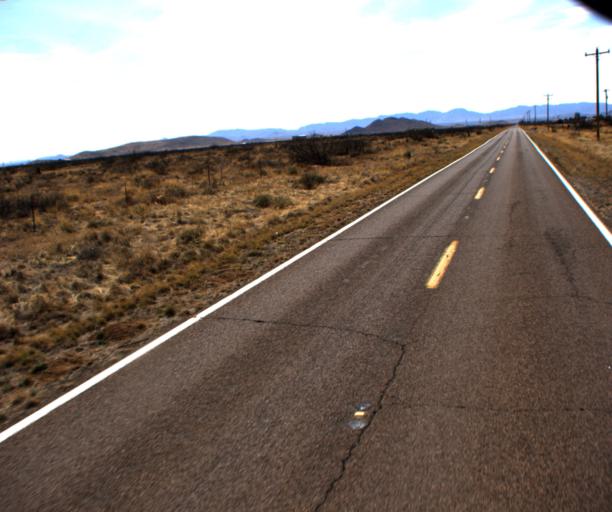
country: US
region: Arizona
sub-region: Cochise County
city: Willcox
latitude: 31.8762
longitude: -109.5956
